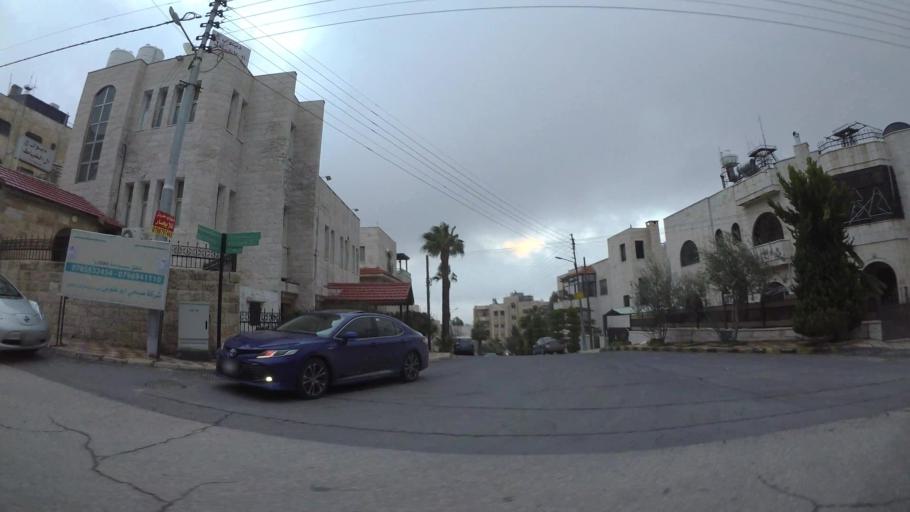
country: JO
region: Amman
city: Al Jubayhah
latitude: 31.9682
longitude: 35.8830
